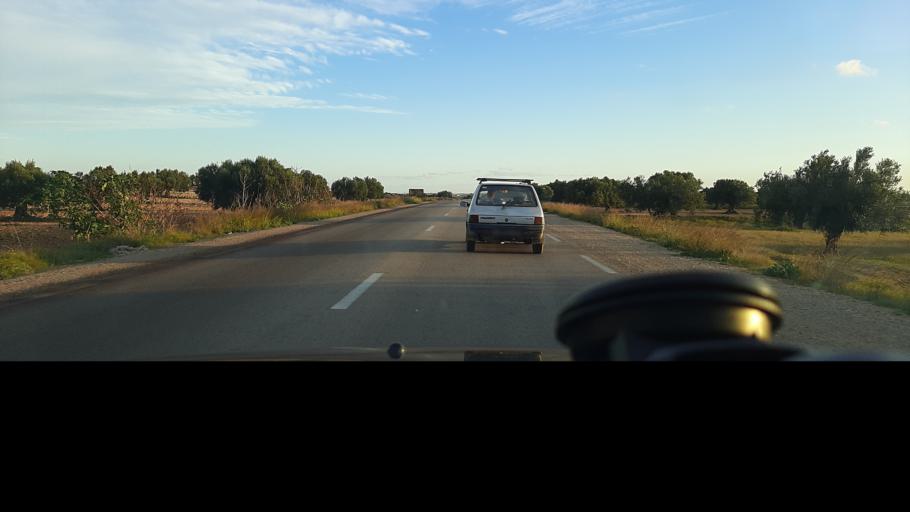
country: TN
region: Safaqis
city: Sfax
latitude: 34.9235
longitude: 10.6263
